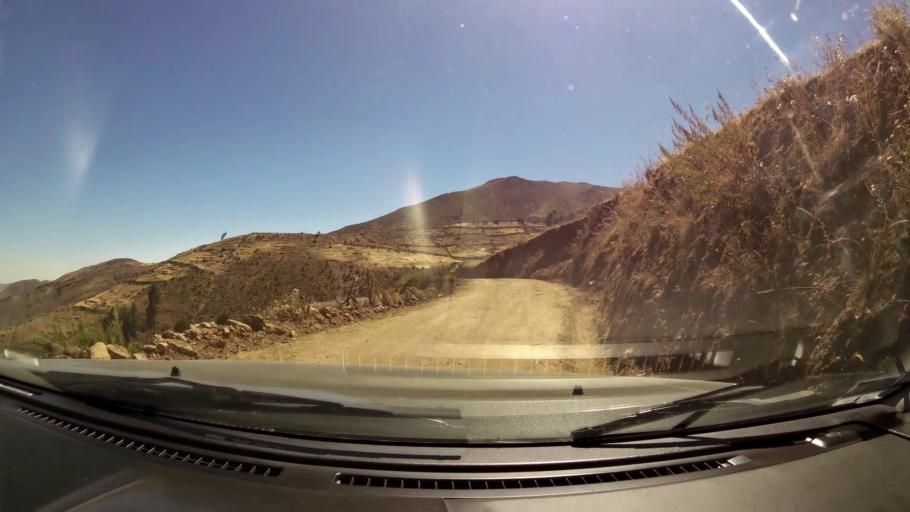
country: PE
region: Huancavelica
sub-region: Huaytara
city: Quito-Arma
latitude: -13.6814
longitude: -75.3779
